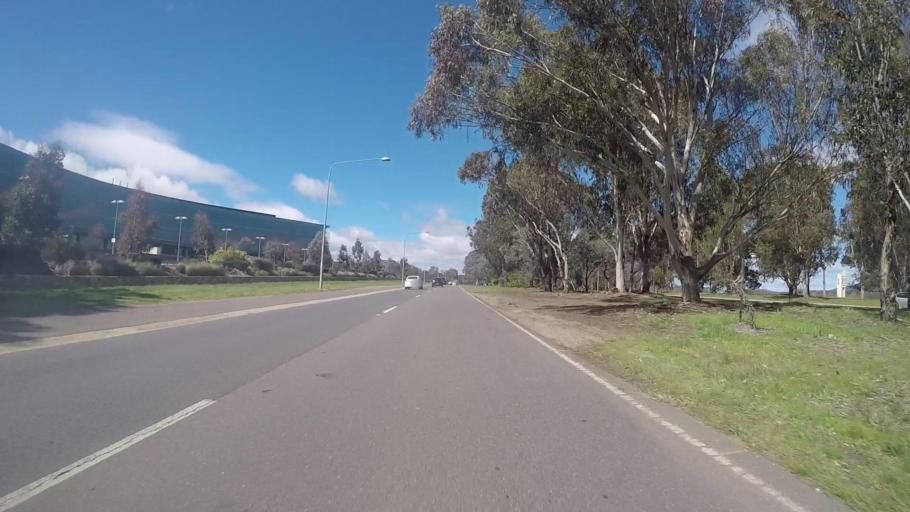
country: AU
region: Australian Capital Territory
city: Canberra
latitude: -35.2926
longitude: 149.1429
